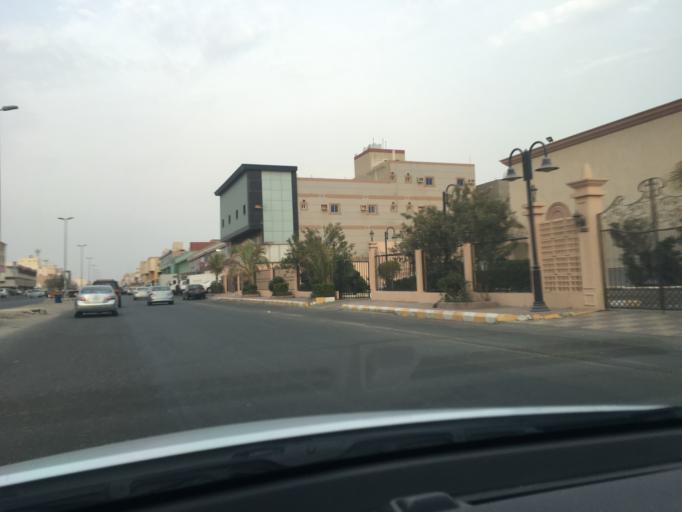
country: SA
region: Makkah
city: Jeddah
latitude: 21.7580
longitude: 39.1883
